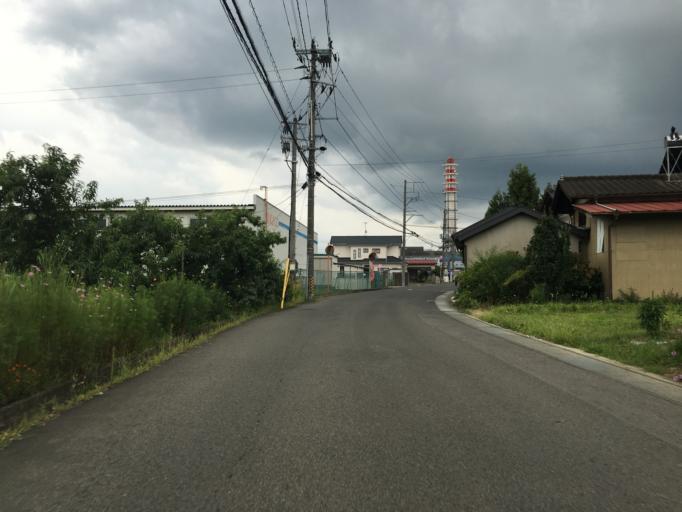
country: JP
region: Fukushima
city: Fukushima-shi
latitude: 37.7478
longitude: 140.4451
